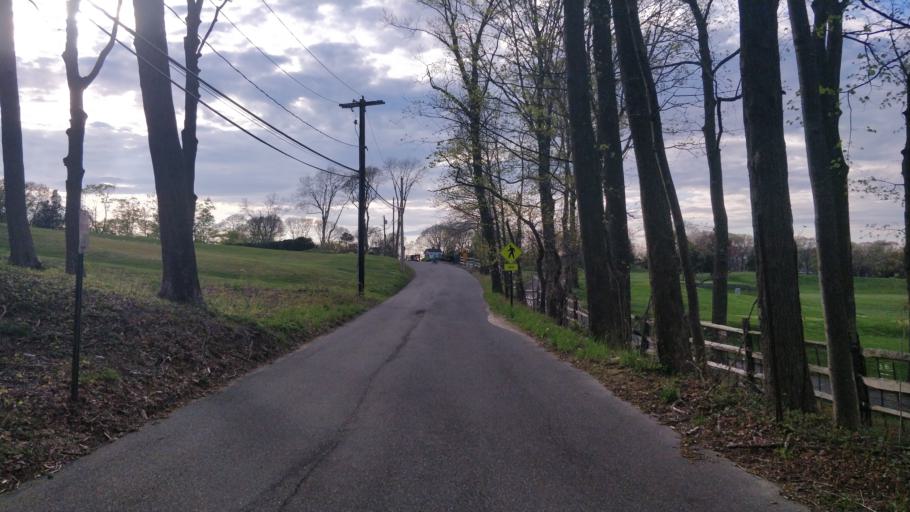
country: US
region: New York
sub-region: Suffolk County
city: Fort Salonga
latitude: 40.9173
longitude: -73.3050
